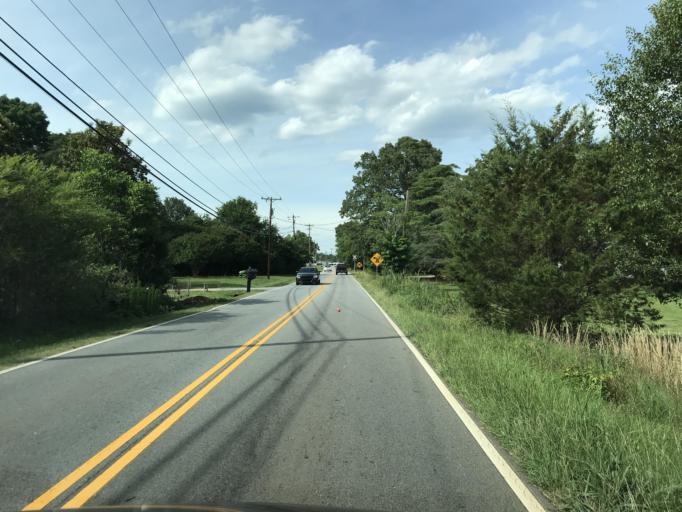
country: US
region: South Carolina
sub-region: Greenville County
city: Gantt
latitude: 34.7824
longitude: -82.4131
